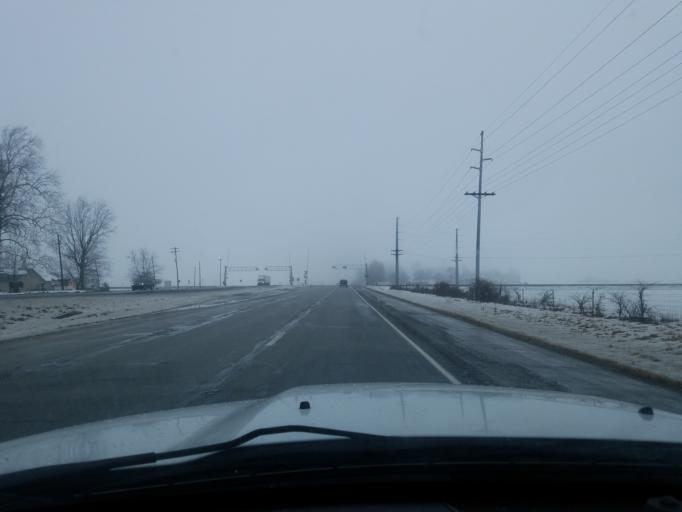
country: US
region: Indiana
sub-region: Tipton County
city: Tipton
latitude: 40.2879
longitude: -86.1268
